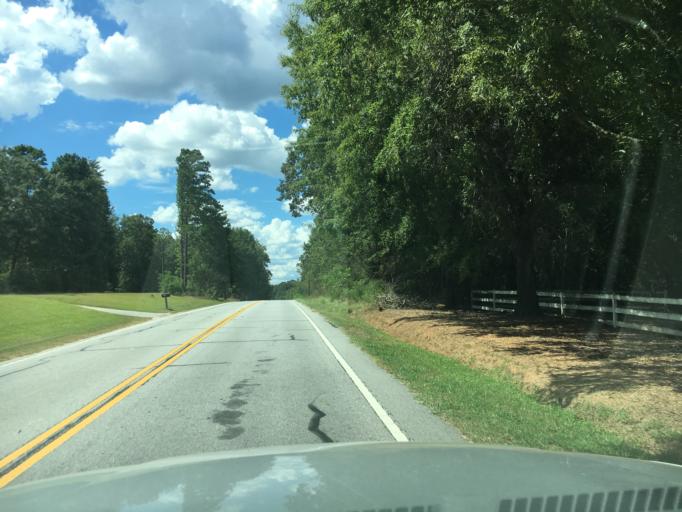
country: US
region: South Carolina
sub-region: Laurens County
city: Laurens
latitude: 34.5205
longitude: -82.1127
